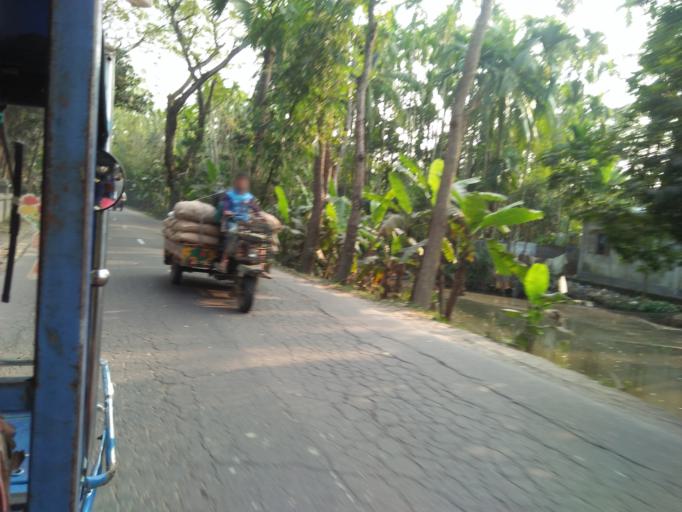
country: BD
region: Barisal
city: Bhola
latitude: 22.7052
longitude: 90.6403
